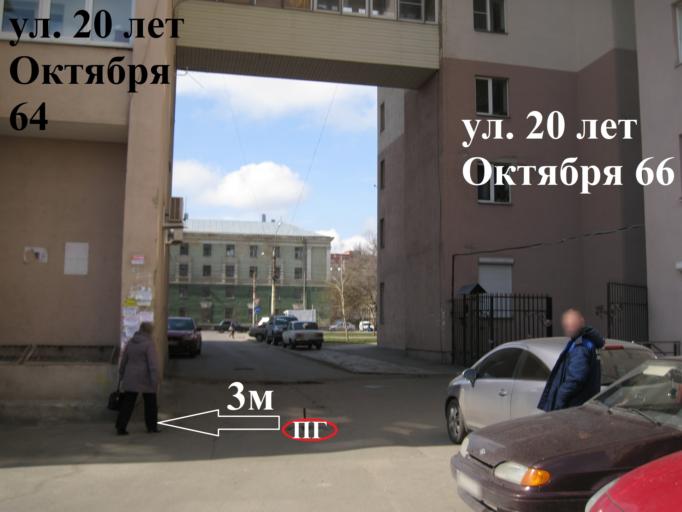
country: RU
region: Voronezj
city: Voronezh
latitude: 51.6486
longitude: 39.1964
